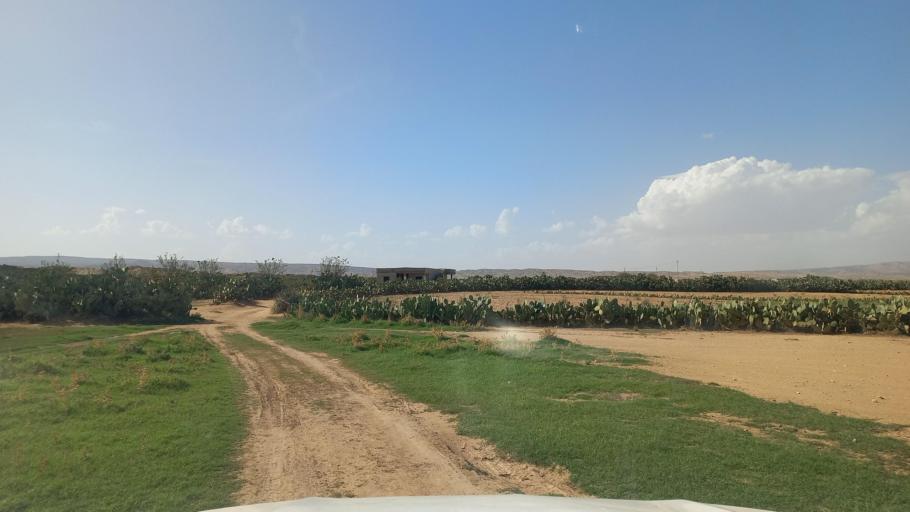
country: TN
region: Al Qasrayn
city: Sbiba
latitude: 35.3174
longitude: 9.0289
